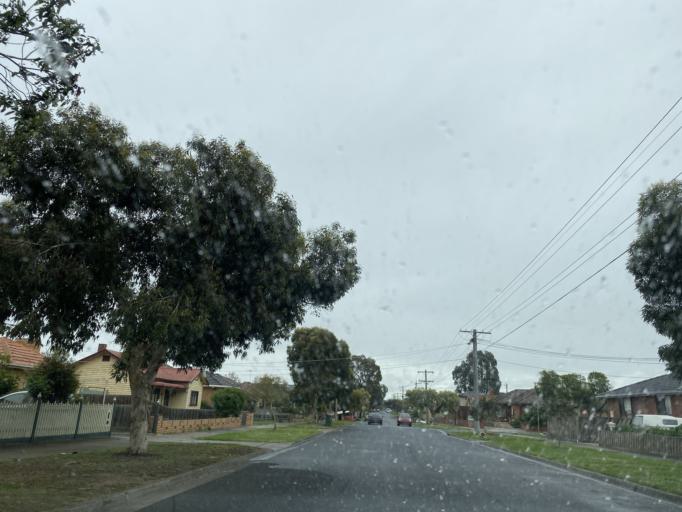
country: AU
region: Victoria
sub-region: Moreland
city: Fawkner
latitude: -37.7118
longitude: 144.9706
